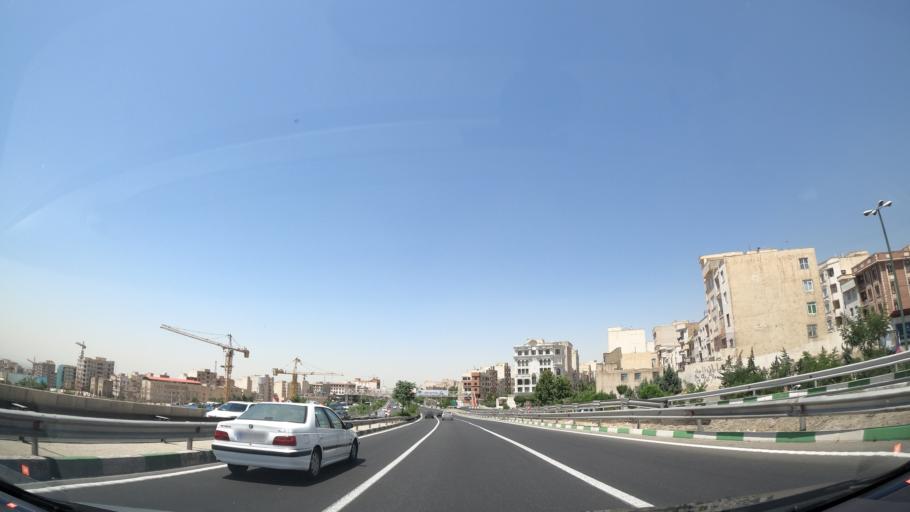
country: IR
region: Tehran
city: Tajrish
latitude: 35.7700
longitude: 51.3157
